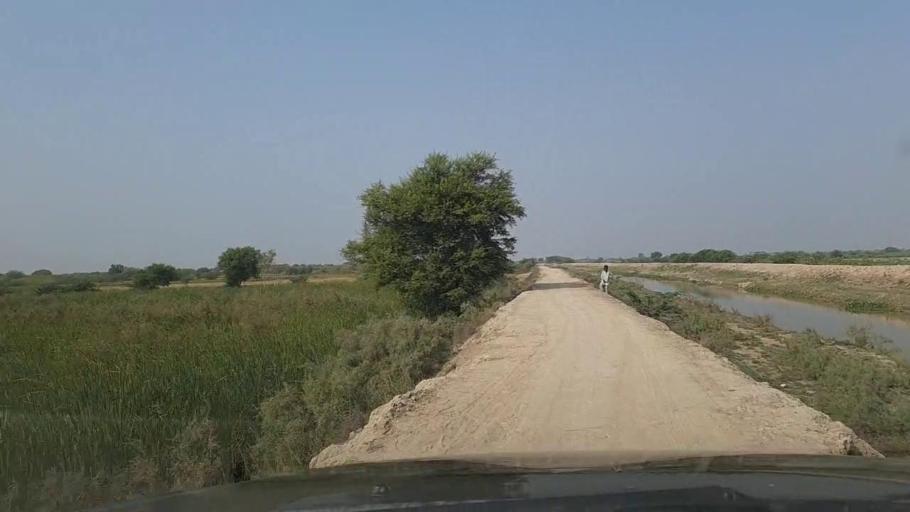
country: PK
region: Sindh
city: Mirpur Batoro
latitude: 24.6826
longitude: 68.2483
